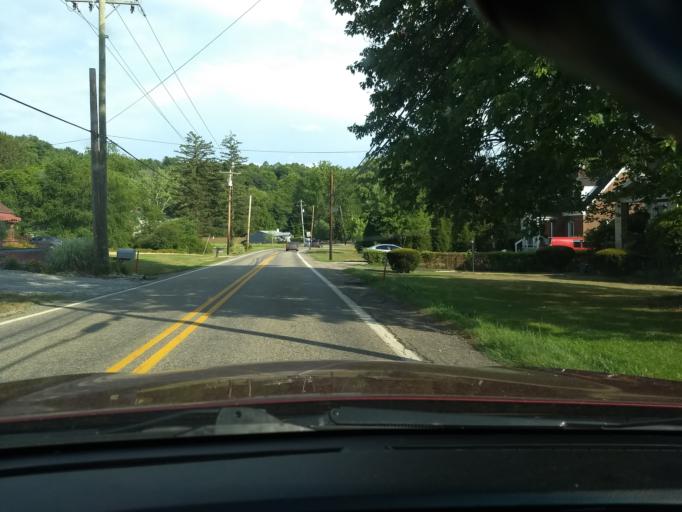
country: US
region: Pennsylvania
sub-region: Allegheny County
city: Tarentum
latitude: 40.6263
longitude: -79.7648
